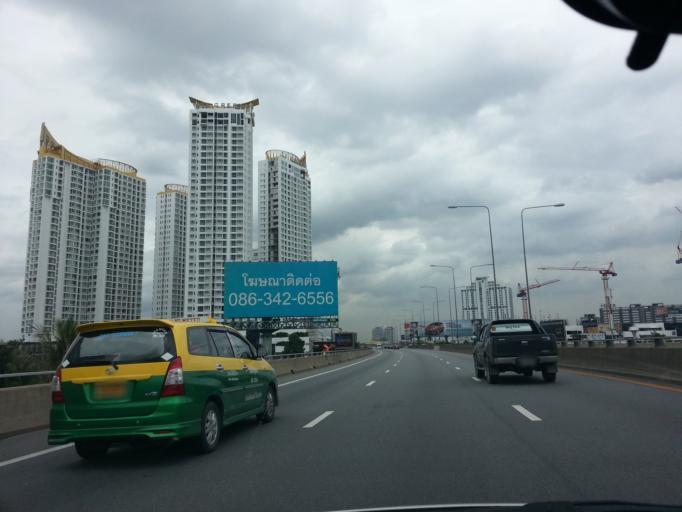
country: TH
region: Bangkok
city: Huai Khwang
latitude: 13.7525
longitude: 100.5728
